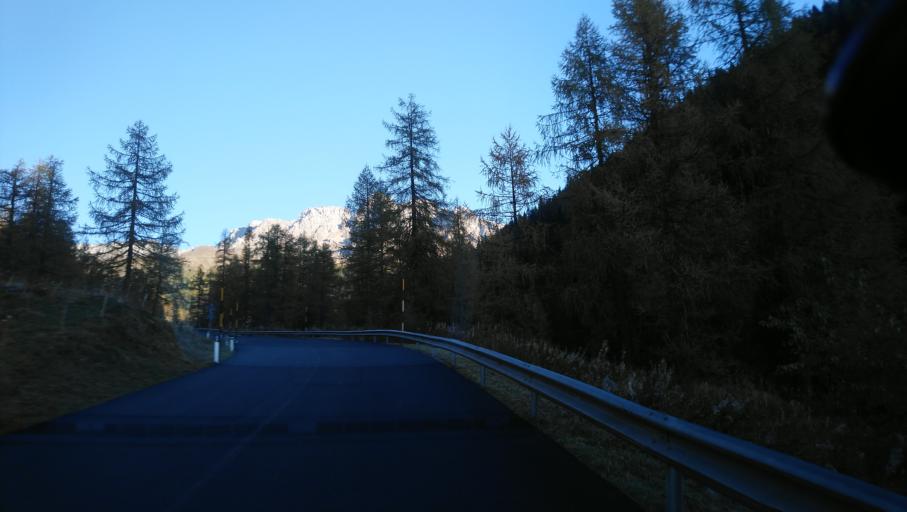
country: IT
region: Veneto
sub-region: Provincia di Belluno
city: Falcade Alto
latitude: 46.3714
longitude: 11.8245
